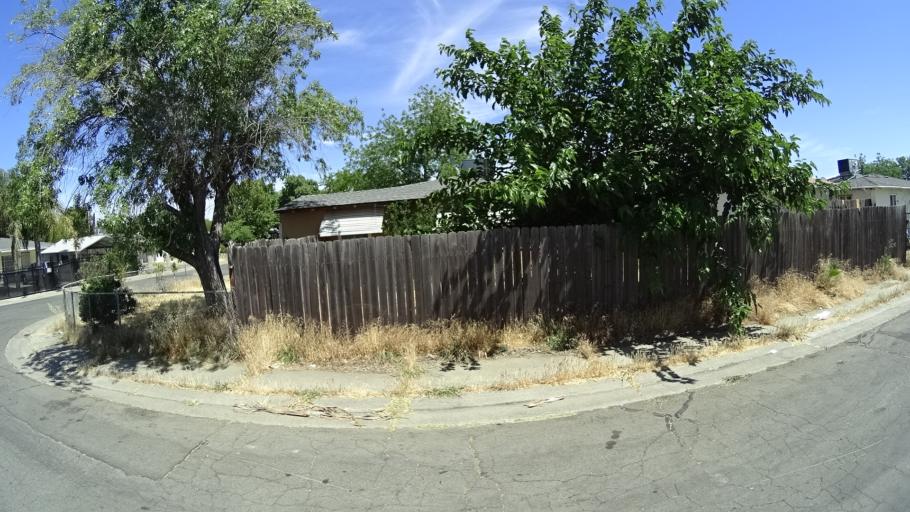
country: US
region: California
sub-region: Sacramento County
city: Florin
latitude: 38.5181
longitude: -121.4240
